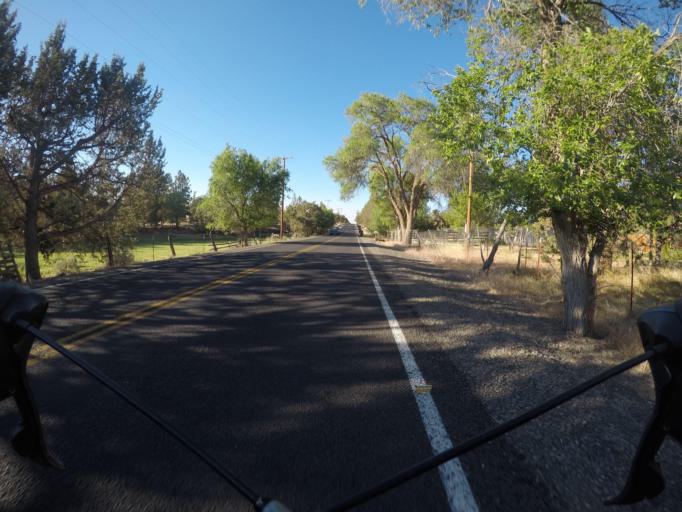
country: US
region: Oregon
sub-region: Deschutes County
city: Redmond
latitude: 44.2494
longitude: -121.2396
